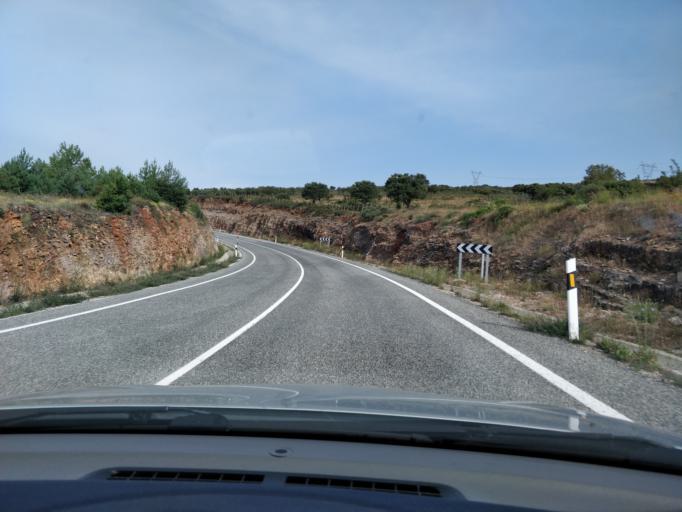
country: ES
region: Castille and Leon
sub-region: Provincia de Burgos
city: Medina de Pomar
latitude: 42.9370
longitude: -3.6602
